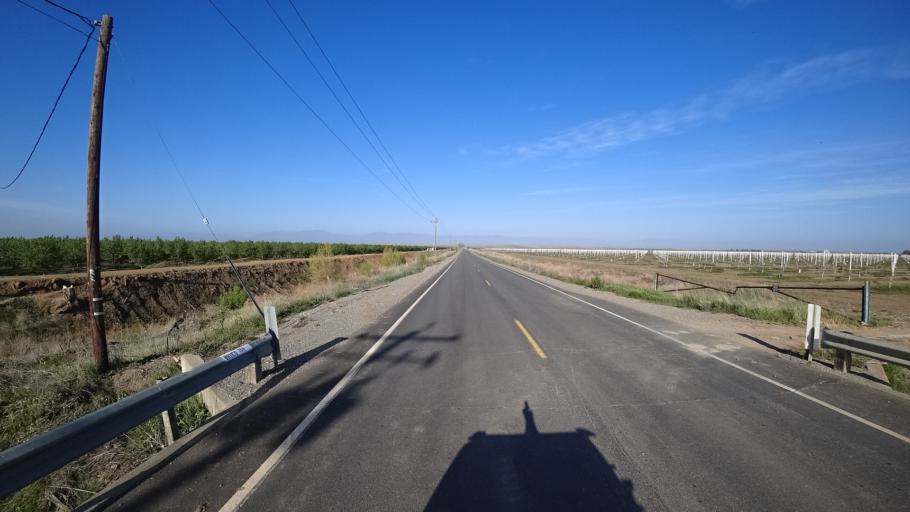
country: US
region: California
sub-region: Glenn County
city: Willows
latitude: 39.5823
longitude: -122.2355
